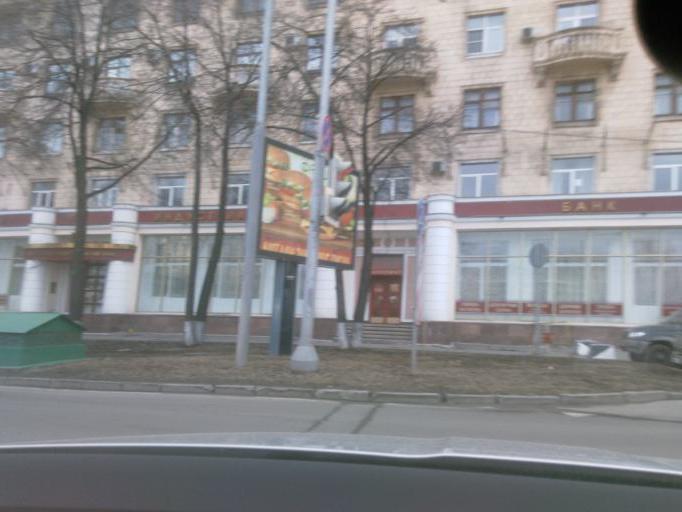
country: RU
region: Moskovskaya
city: Dorogomilovo
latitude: 55.7475
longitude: 37.5762
